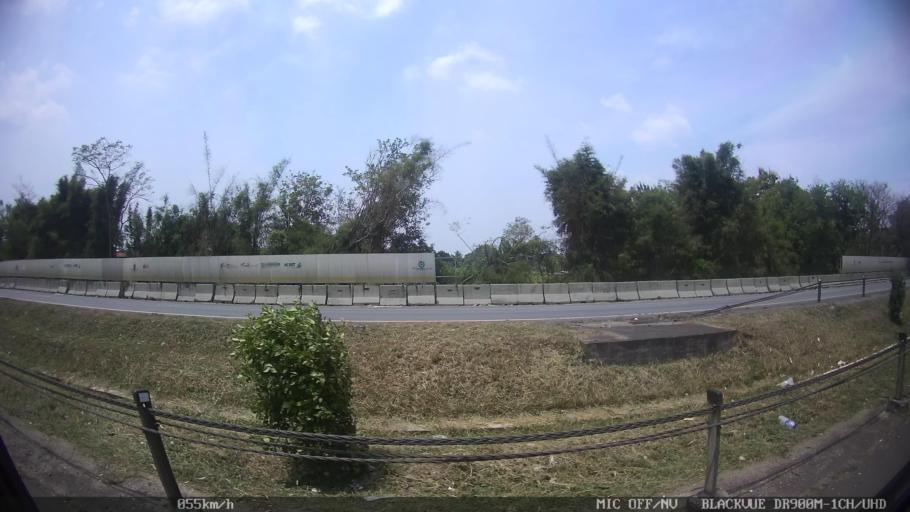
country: ID
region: Banten
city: Serang
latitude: -6.1257
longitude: 106.1914
